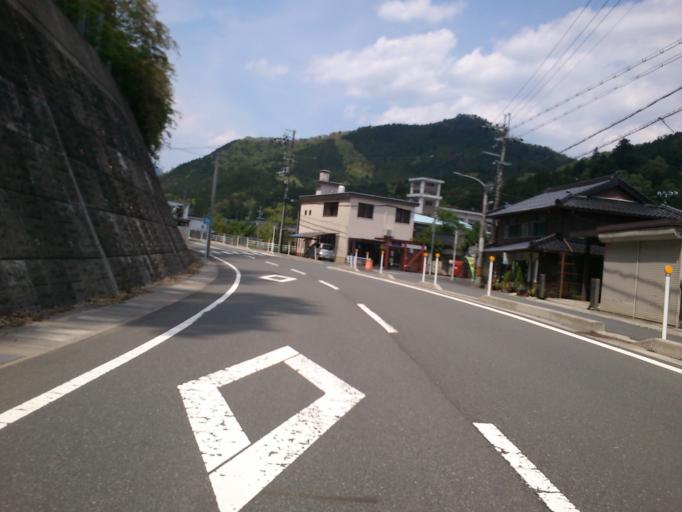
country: JP
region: Kyoto
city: Fukuchiyama
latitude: 35.3498
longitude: 134.9451
